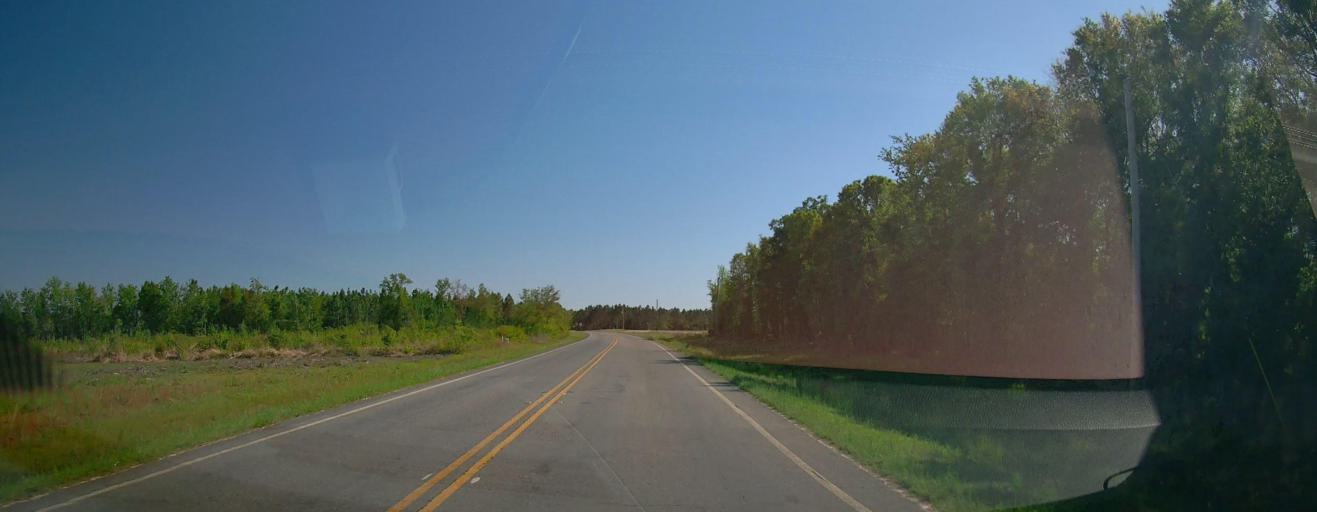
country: US
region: Georgia
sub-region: Wilcox County
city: Rochelle
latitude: 32.1001
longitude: -83.5027
